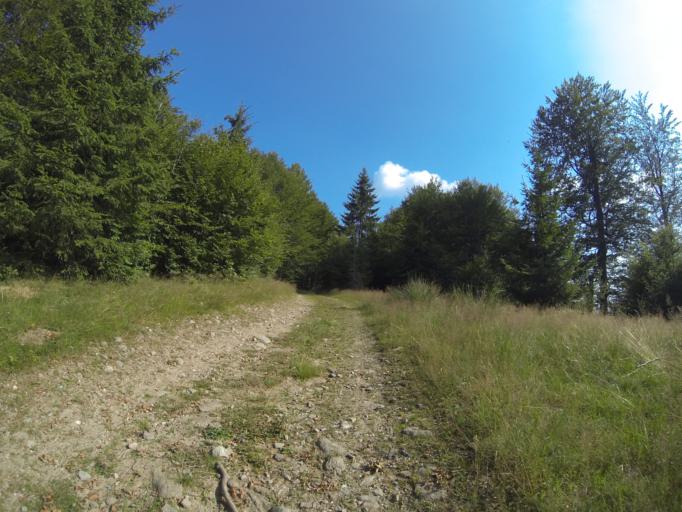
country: RO
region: Valcea
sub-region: Comuna Vaideeni
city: Vaideeni
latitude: 45.2403
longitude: 23.9584
